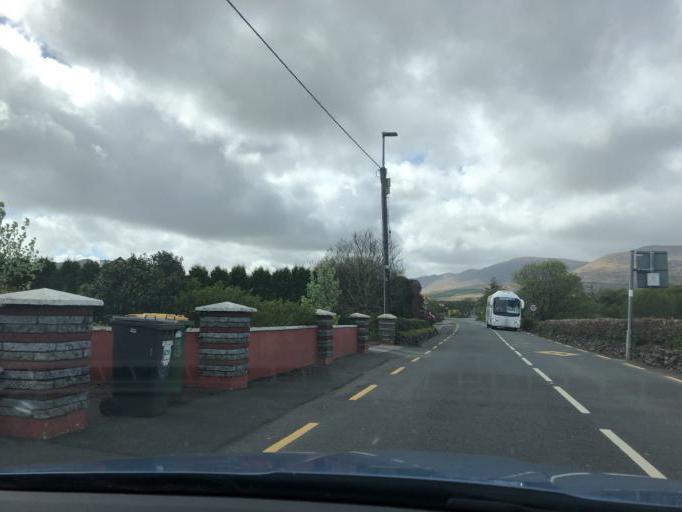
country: IE
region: Munster
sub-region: Ciarrai
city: Killorglin
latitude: 51.8388
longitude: -9.9055
